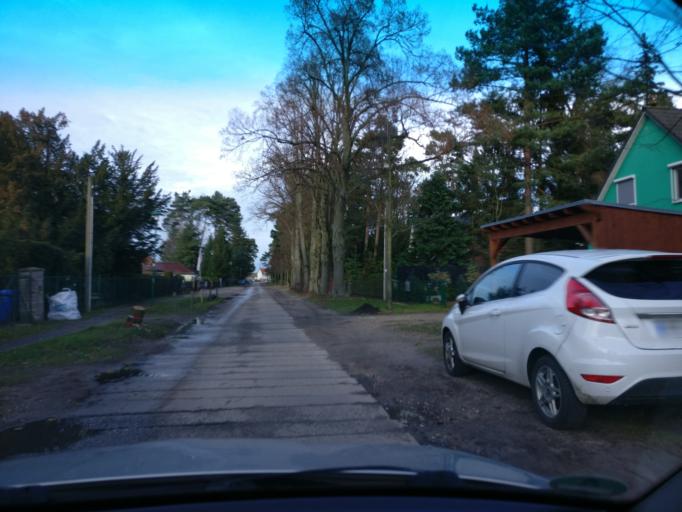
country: DE
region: Brandenburg
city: Bernau bei Berlin
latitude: 52.6721
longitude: 13.5410
